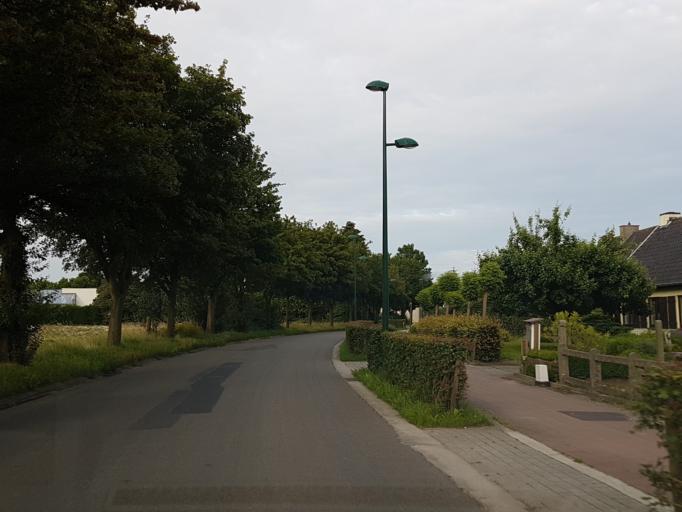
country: BE
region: Flanders
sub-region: Provincie Oost-Vlaanderen
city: Aalst
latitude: 50.9364
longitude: 4.0714
